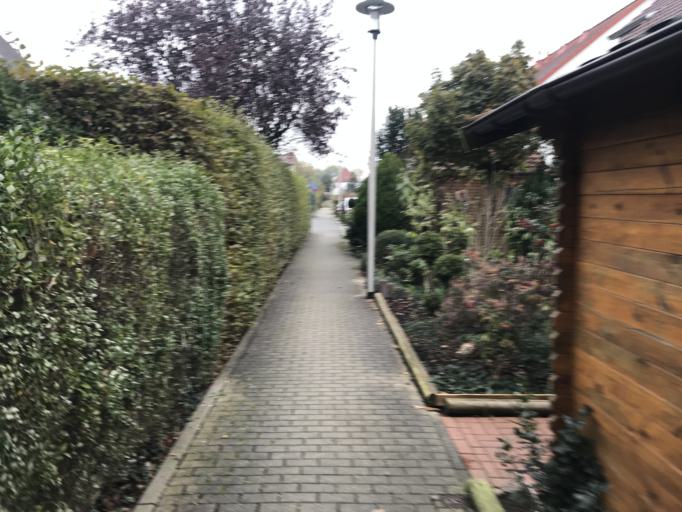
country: DE
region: North Rhine-Westphalia
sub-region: Regierungsbezirk Arnsberg
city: Hamm
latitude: 51.6887
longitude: 7.8655
